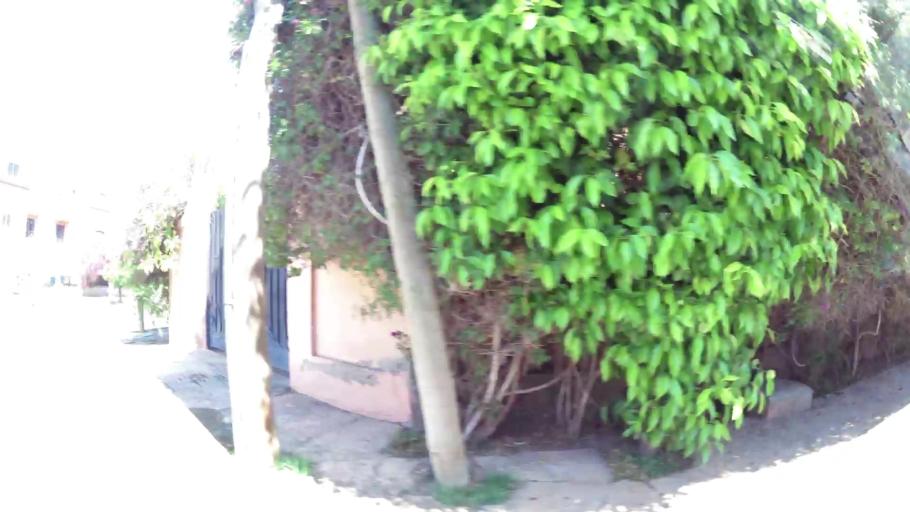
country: MA
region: Marrakech-Tensift-Al Haouz
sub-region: Marrakech
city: Marrakesh
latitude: 31.6485
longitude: -8.0614
